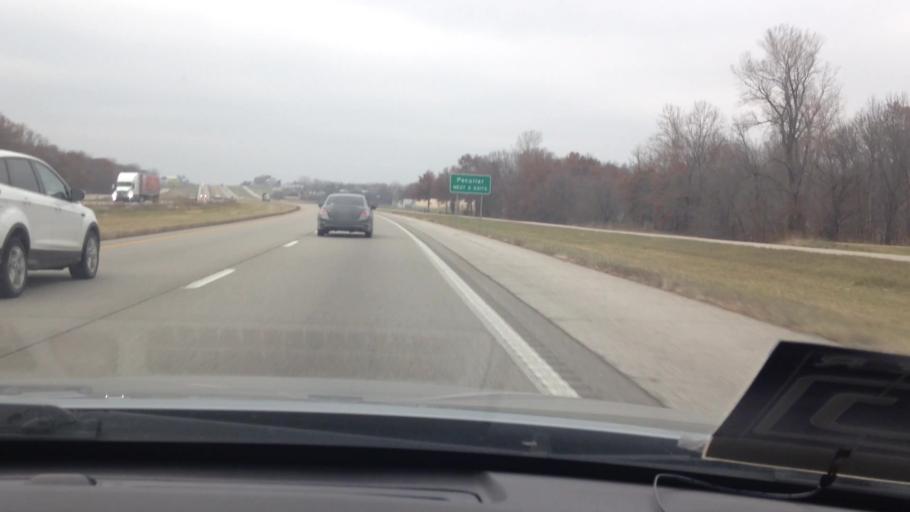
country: US
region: Missouri
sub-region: Cass County
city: Peculiar
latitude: 38.6970
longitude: -94.4300
